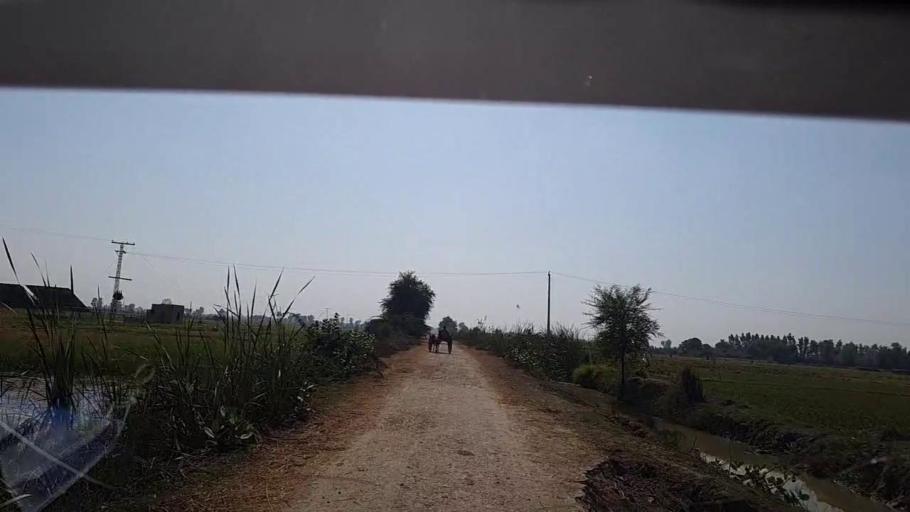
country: PK
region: Sindh
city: Naudero
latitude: 27.6967
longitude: 68.4022
